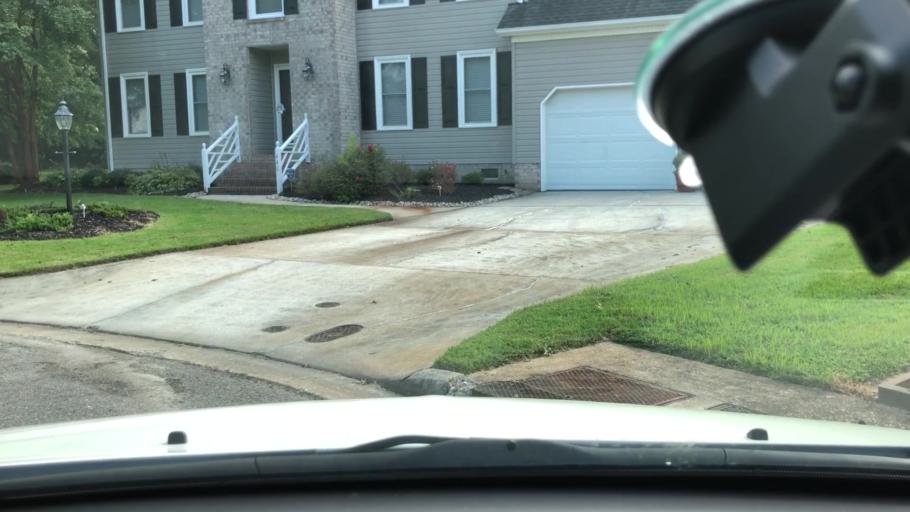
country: US
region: Virginia
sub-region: City of Chesapeake
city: Chesapeake
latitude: 36.7059
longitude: -76.2838
